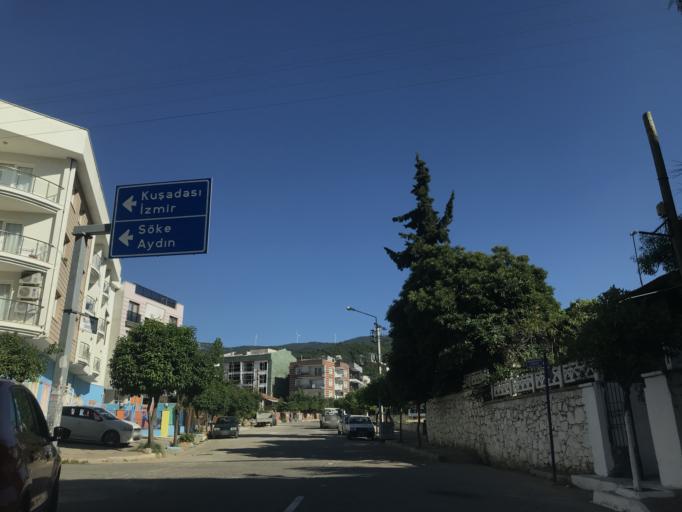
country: TR
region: Aydin
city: Davutlar
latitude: 37.7327
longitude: 27.2865
